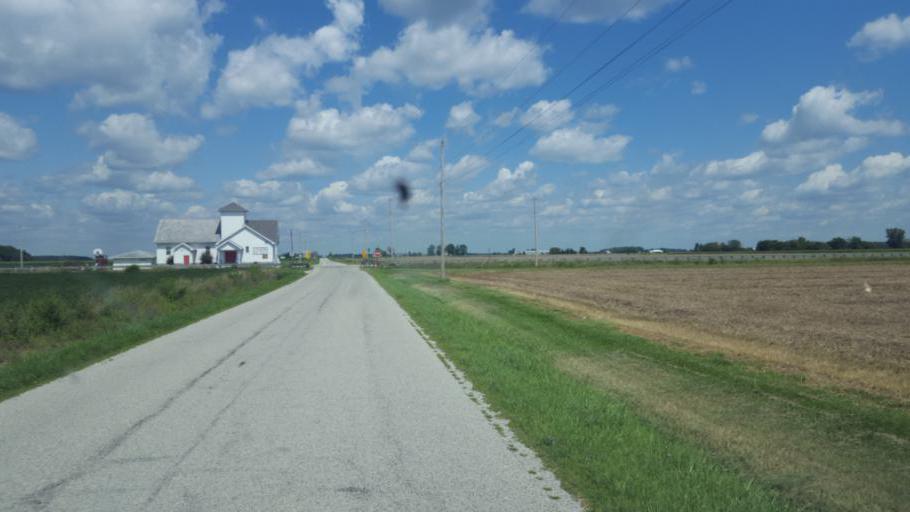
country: US
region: Ohio
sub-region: Sandusky County
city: Gibsonburg
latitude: 41.2538
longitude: -83.3225
